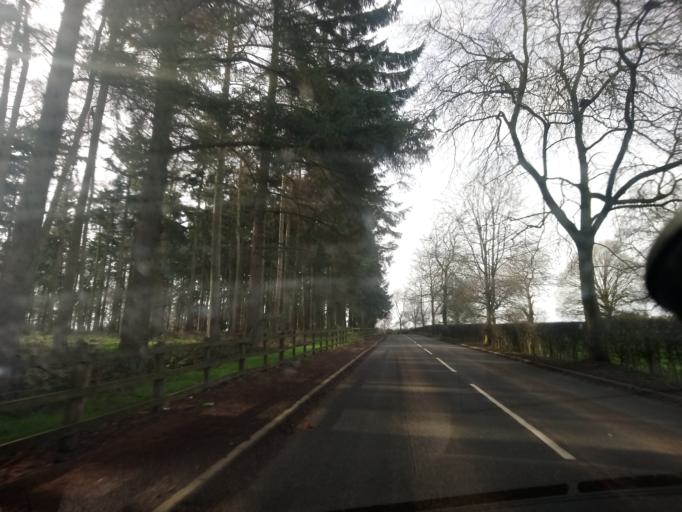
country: GB
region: England
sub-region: Shropshire
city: Stoke upon Tern
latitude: 52.8545
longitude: -2.5812
